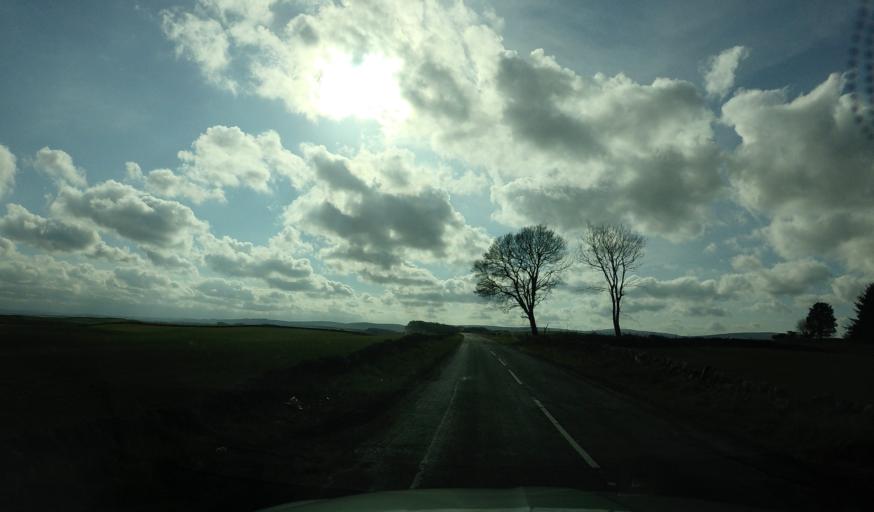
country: GB
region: Scotland
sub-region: Midlothian
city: Penicuik
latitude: 55.8073
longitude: -3.1804
